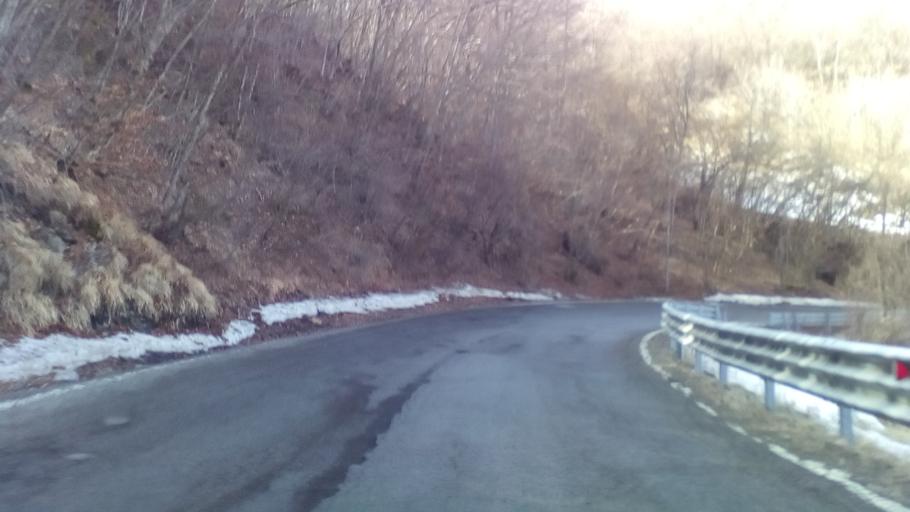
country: IT
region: Emilia-Romagna
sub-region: Provincia di Modena
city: Riolunato
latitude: 44.2495
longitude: 10.6325
